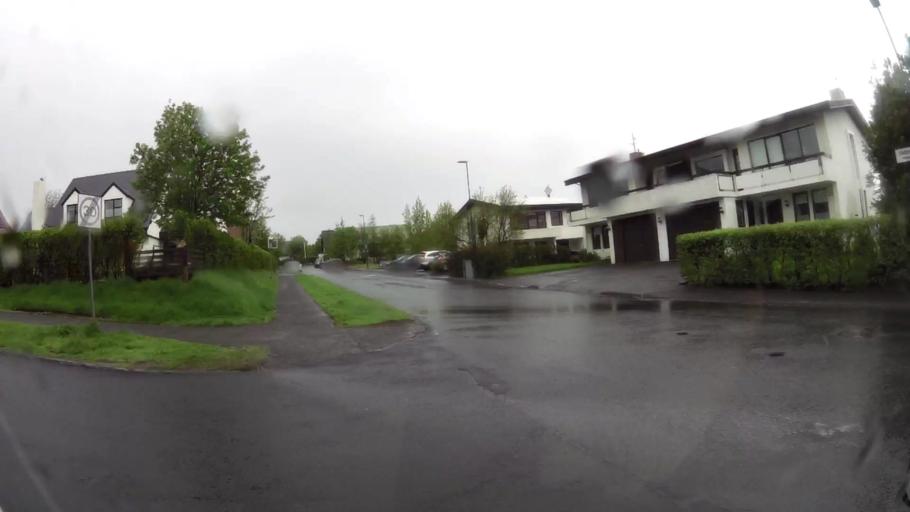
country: IS
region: Capital Region
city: Reykjavik
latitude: 64.0962
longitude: -21.8454
